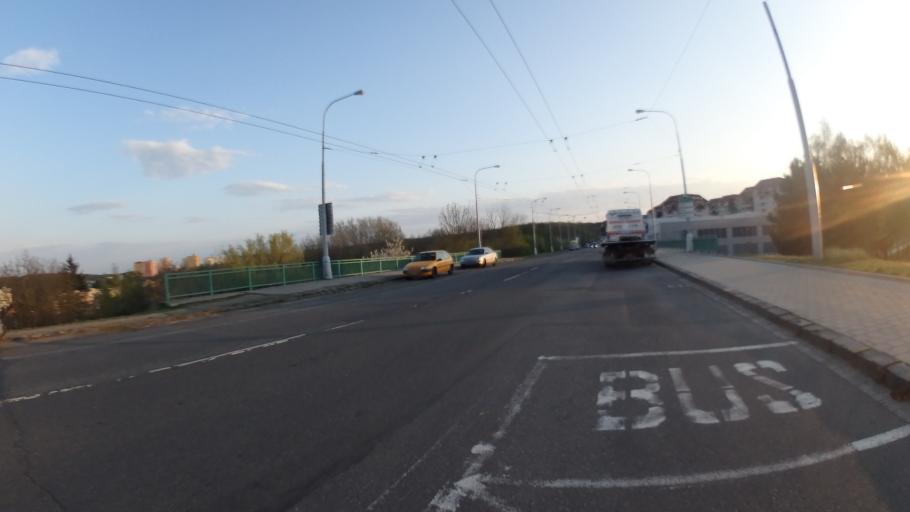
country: CZ
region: South Moravian
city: Troubsko
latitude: 49.1965
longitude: 16.5342
